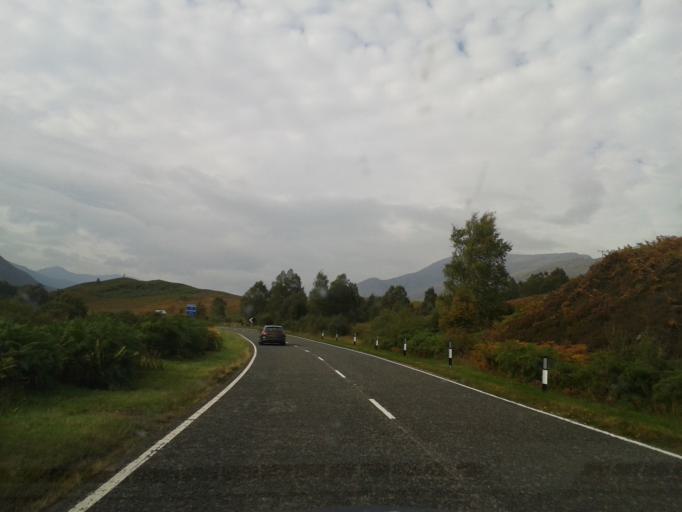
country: GB
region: Scotland
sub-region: Highland
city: Spean Bridge
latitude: 57.1457
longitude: -4.9734
